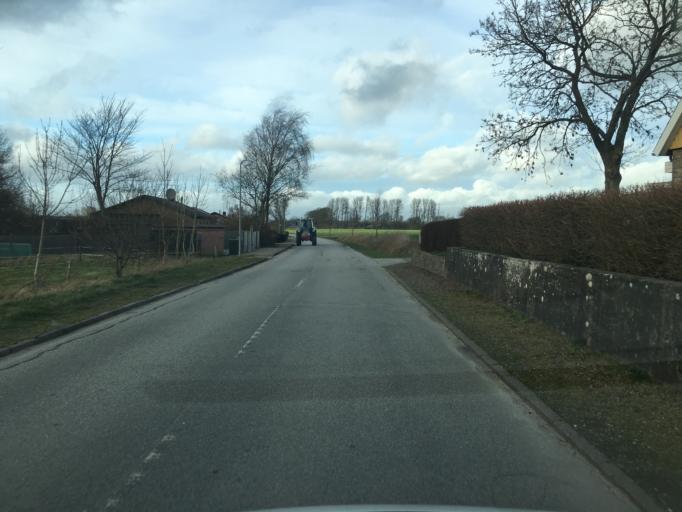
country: DK
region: South Denmark
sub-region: Sonderborg Kommune
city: Grasten
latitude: 54.9725
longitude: 9.5171
